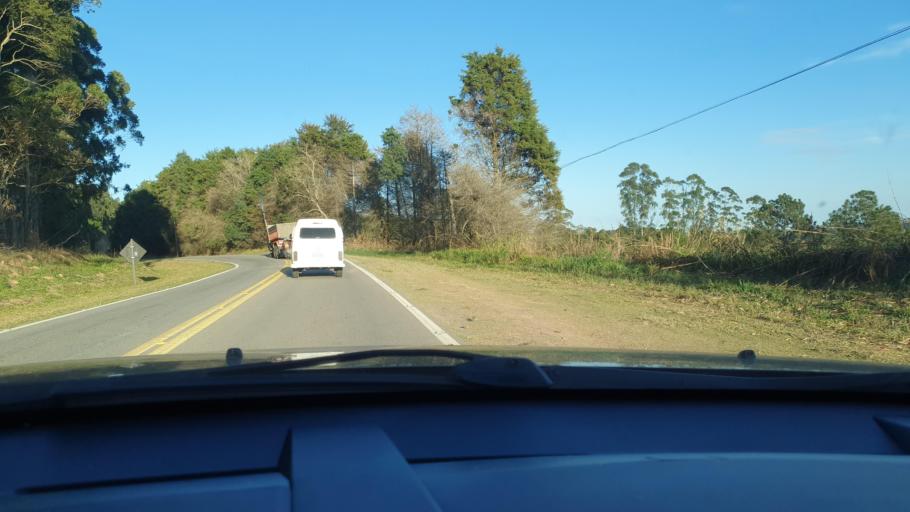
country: BR
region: Sao Paulo
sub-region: Piedade
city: Piedade
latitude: -23.7171
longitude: -47.3849
